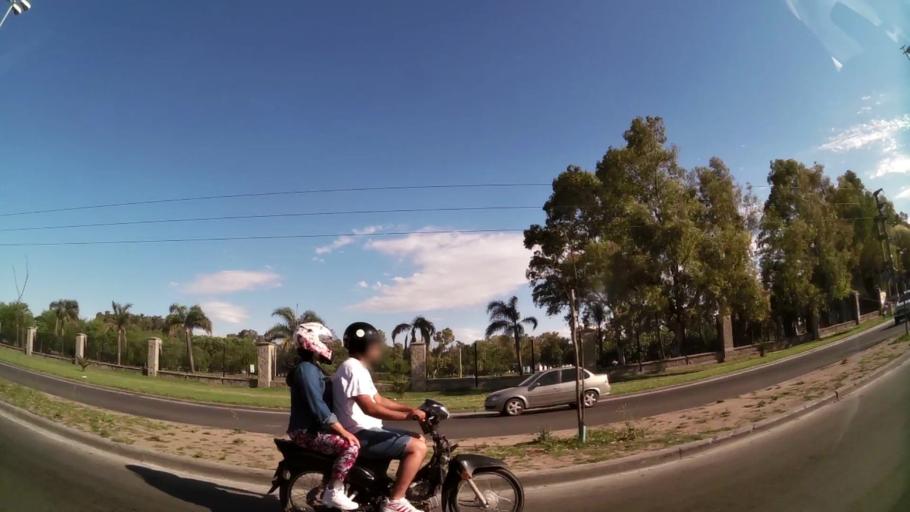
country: AR
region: Buenos Aires
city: Santa Catalina - Dique Lujan
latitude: -34.4911
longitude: -58.7009
